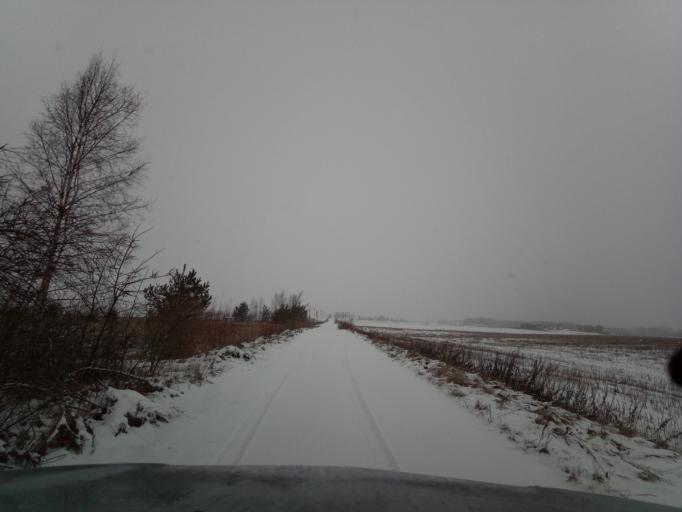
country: LT
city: Ramygala
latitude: 55.5876
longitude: 24.3663
